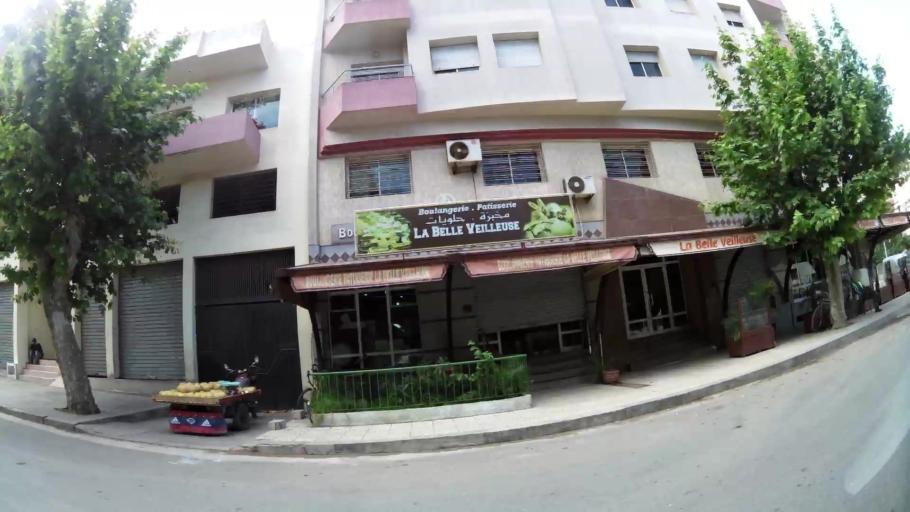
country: MA
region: Gharb-Chrarda-Beni Hssen
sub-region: Kenitra Province
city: Kenitra
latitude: 34.2552
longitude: -6.5845
